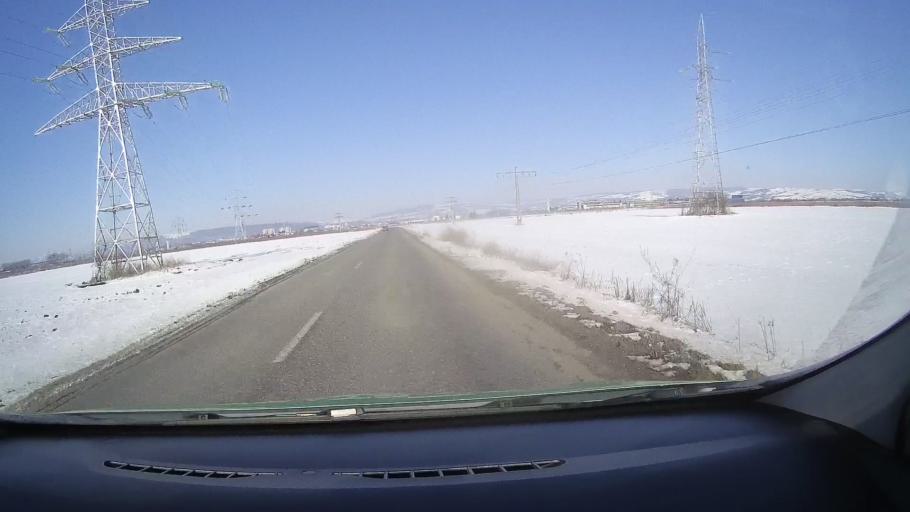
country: RO
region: Brasov
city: Fogarasch
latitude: 45.8155
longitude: 24.9877
